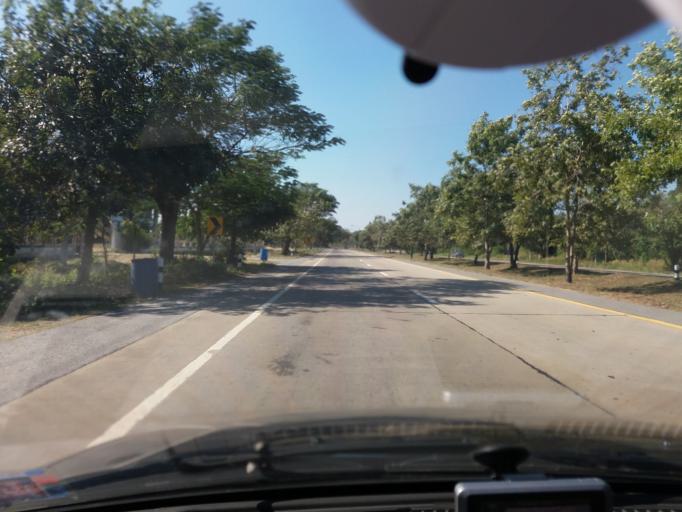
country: TH
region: Suphan Buri
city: Sam Chuk
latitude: 14.7930
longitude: 100.1059
